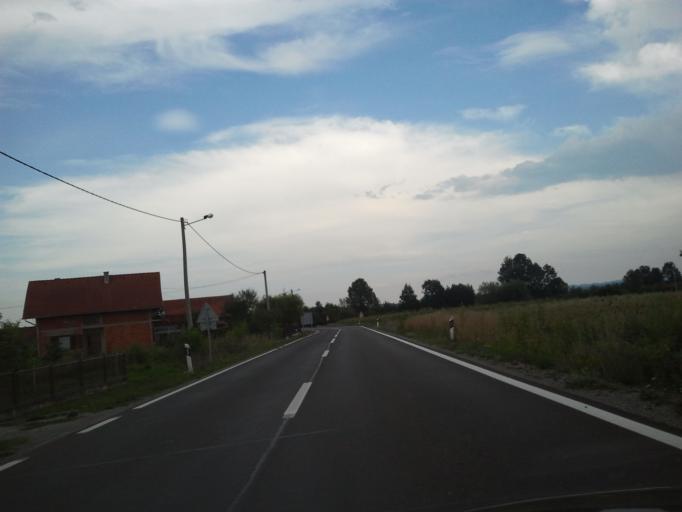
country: HR
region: Sisacko-Moslavacka
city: Glina
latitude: 45.3417
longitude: 16.0654
